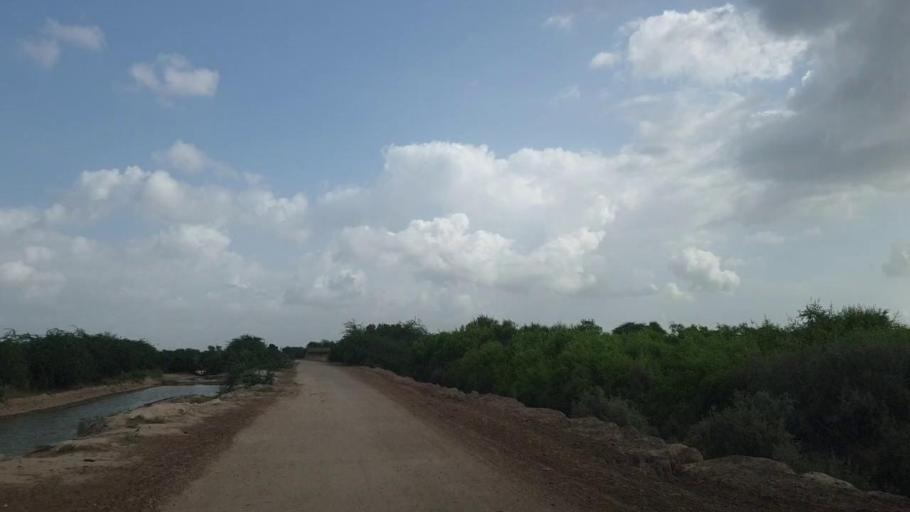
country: PK
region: Sindh
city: Kadhan
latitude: 24.5515
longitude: 69.0635
